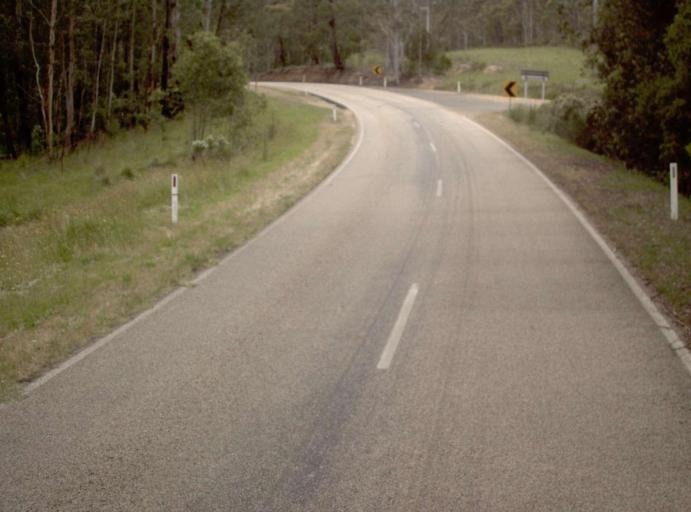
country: AU
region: Victoria
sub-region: East Gippsland
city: Bairnsdale
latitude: -37.6272
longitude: 147.2075
